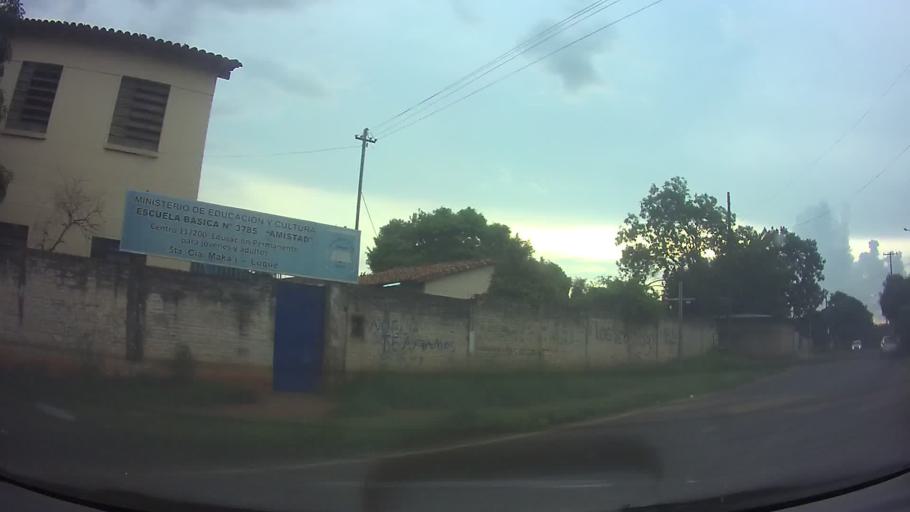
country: PY
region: Central
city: San Lorenzo
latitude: -25.2799
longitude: -57.4806
